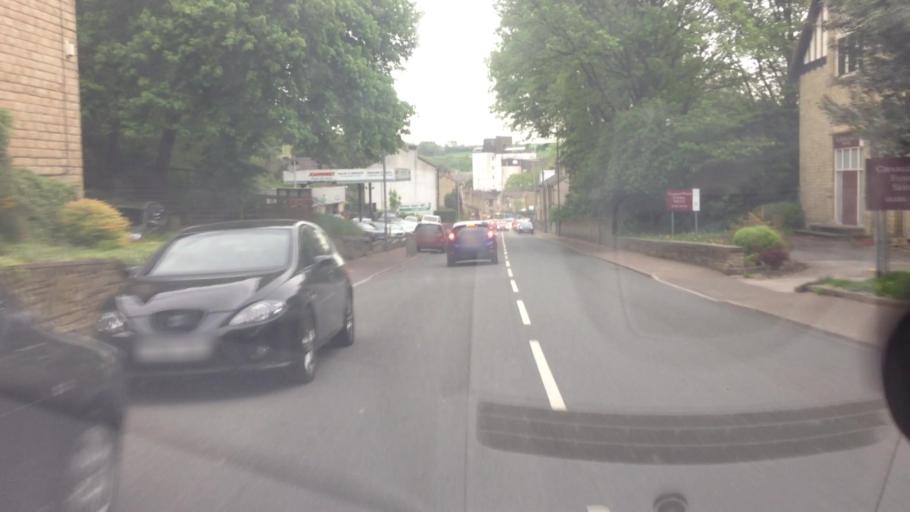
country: GB
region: England
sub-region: Calderdale
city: Brighouse
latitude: 53.6966
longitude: -1.7867
